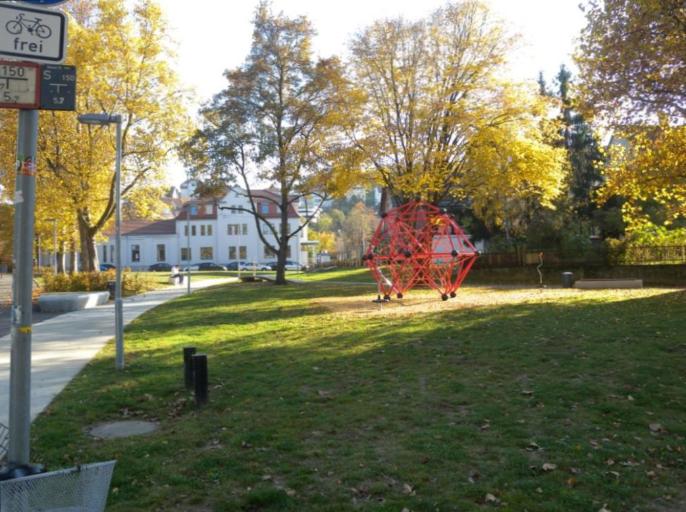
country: DE
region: Baden-Wuerttemberg
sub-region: Regierungsbezirk Stuttgart
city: Stuttgart Feuerbach
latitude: 48.8129
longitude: 9.1692
